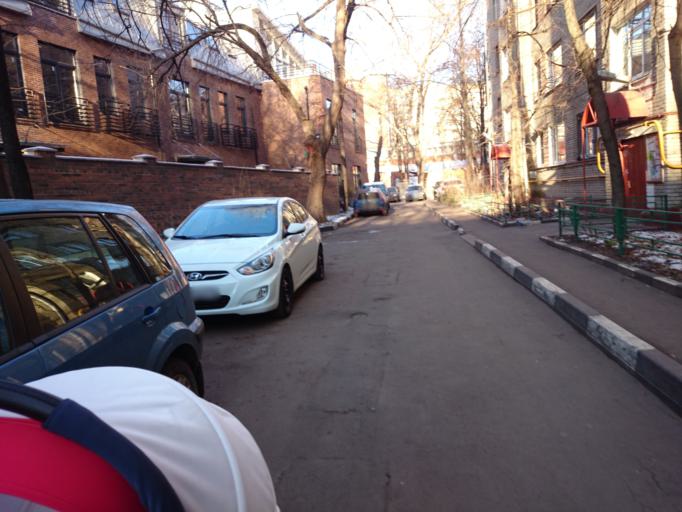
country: RU
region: Moscow
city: Sokol
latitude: 55.7974
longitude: 37.5231
